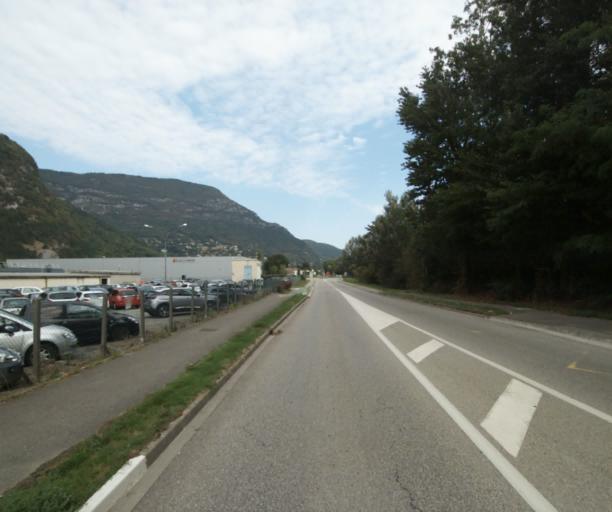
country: FR
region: Rhone-Alpes
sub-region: Departement de l'Isere
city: Noyarey
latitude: 45.2620
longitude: 5.6247
